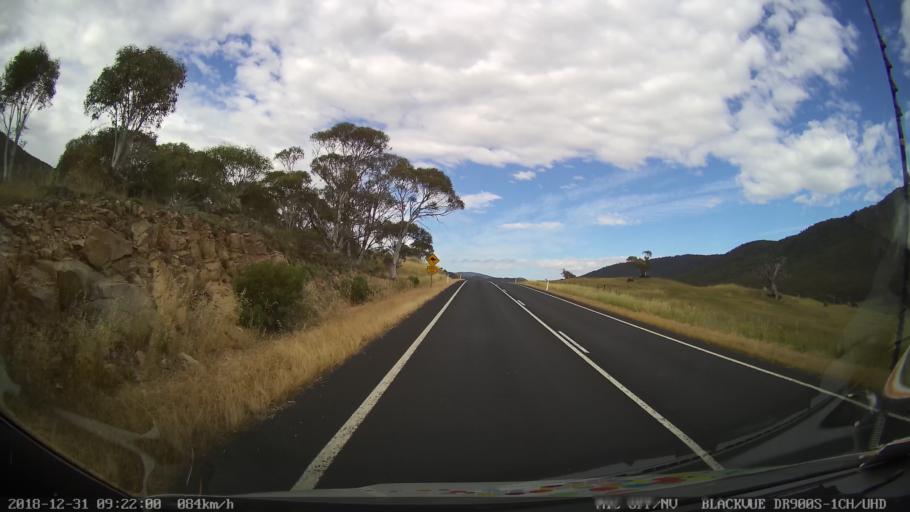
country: AU
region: New South Wales
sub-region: Snowy River
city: Jindabyne
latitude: -36.4318
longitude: 148.5537
